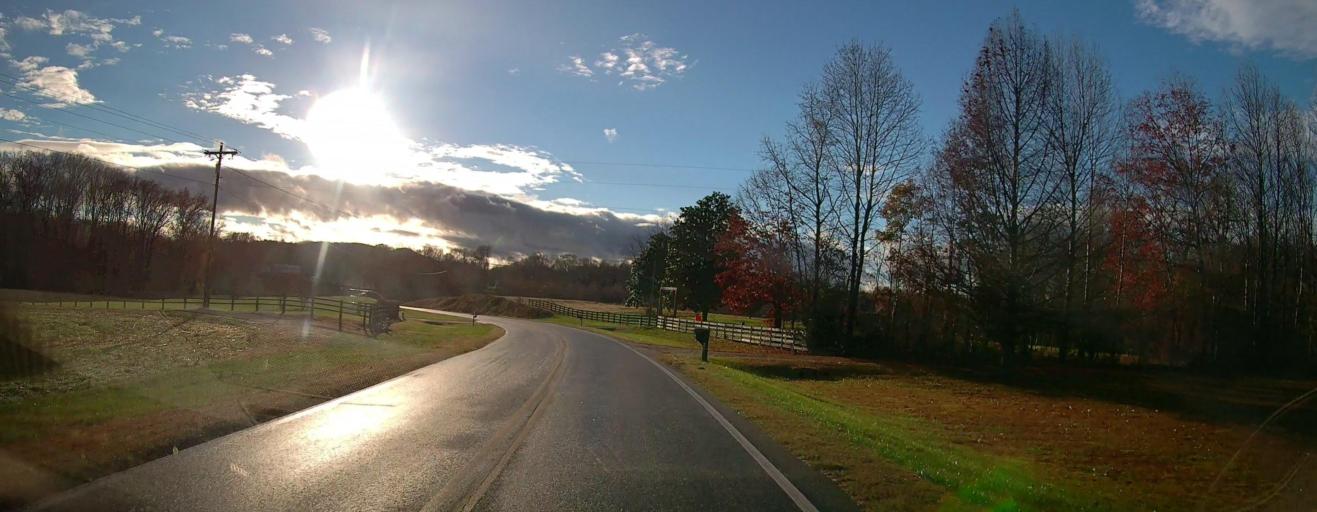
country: US
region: Georgia
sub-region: White County
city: Cleveland
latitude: 34.5465
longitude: -83.7095
